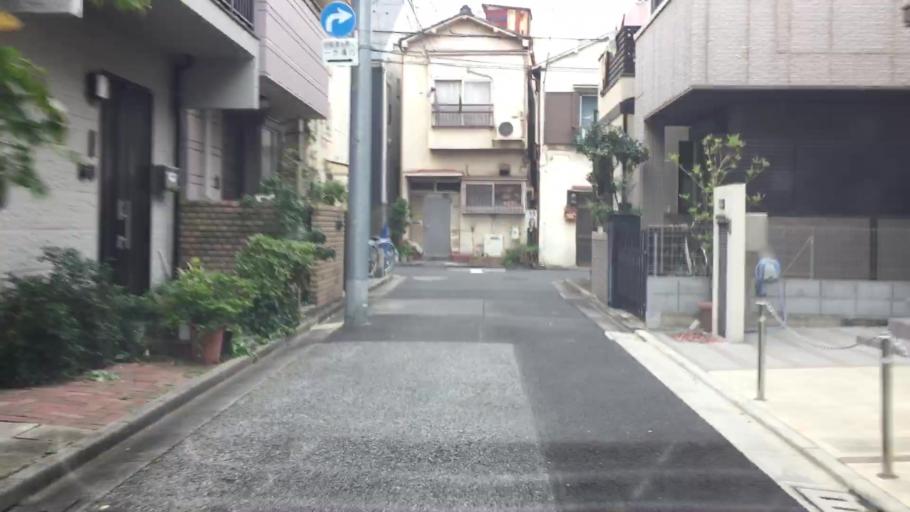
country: JP
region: Saitama
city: Soka
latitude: 35.7489
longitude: 139.7779
